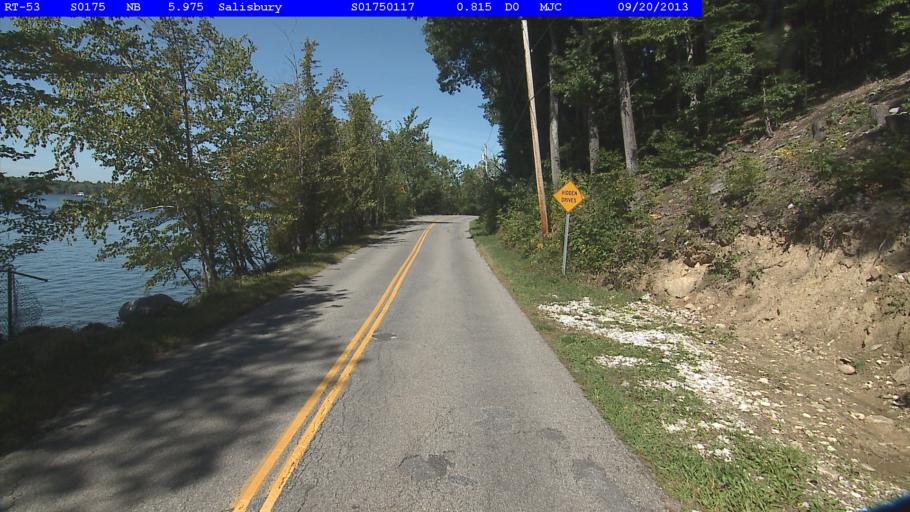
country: US
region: Vermont
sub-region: Rutland County
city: Brandon
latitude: 43.9092
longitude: -73.0665
